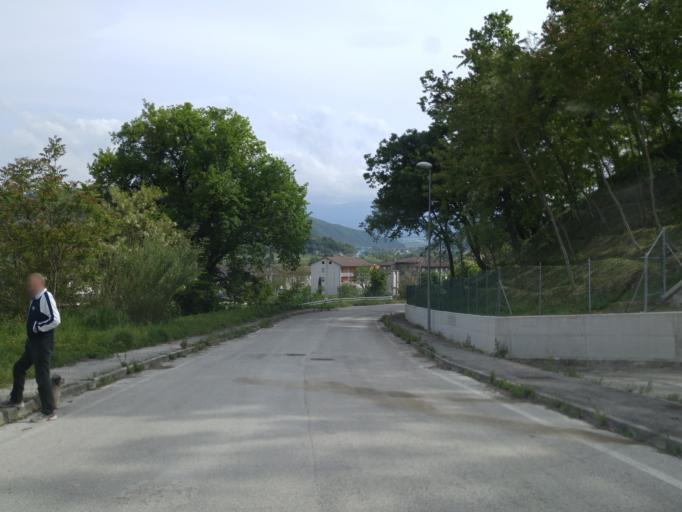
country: IT
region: The Marches
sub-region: Provincia di Pesaro e Urbino
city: Acqualagna
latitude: 43.6290
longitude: 12.6758
